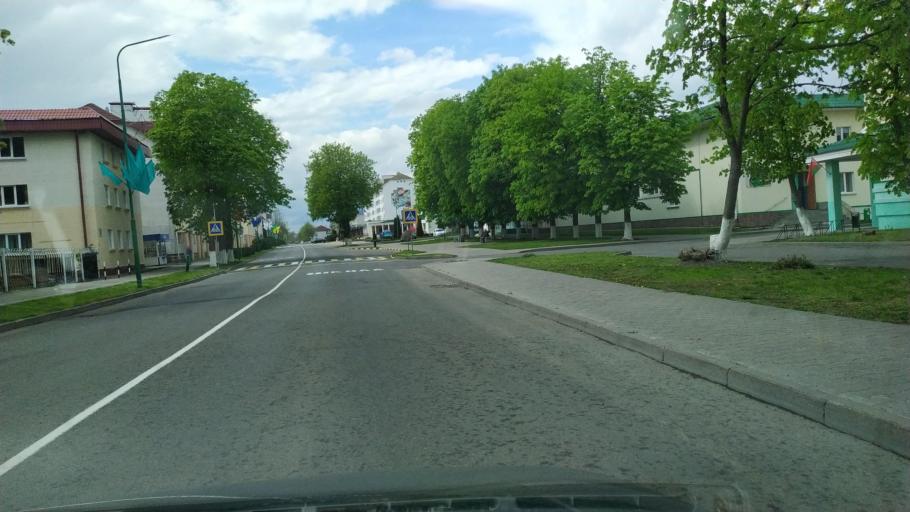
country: BY
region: Brest
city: Pruzhany
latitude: 52.5544
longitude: 24.4648
